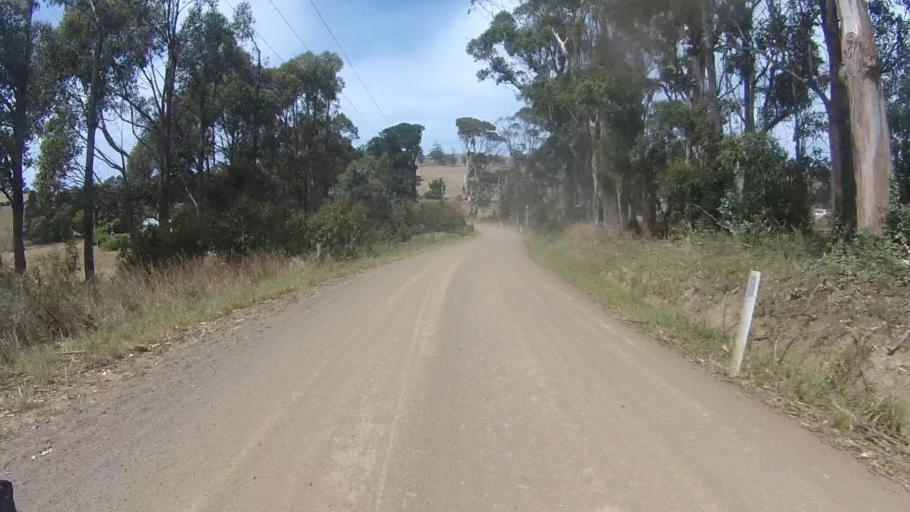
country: AU
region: Tasmania
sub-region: Sorell
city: Sorell
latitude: -42.8193
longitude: 147.8239
